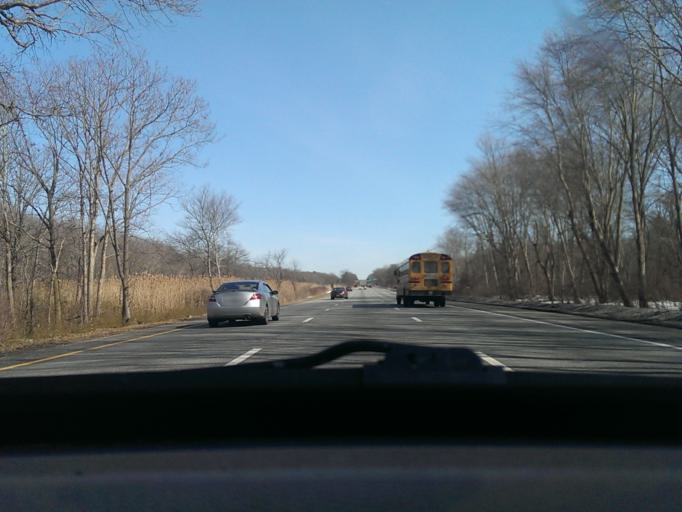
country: US
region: Rhode Island
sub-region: Bristol County
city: Warren
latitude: 41.7774
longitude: -71.2746
